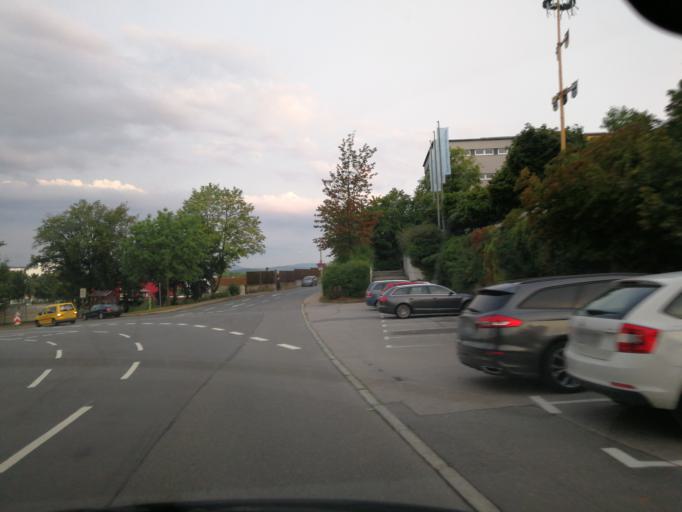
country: DE
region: Bavaria
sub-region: Upper Palatinate
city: Cham
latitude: 49.2254
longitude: 12.6683
